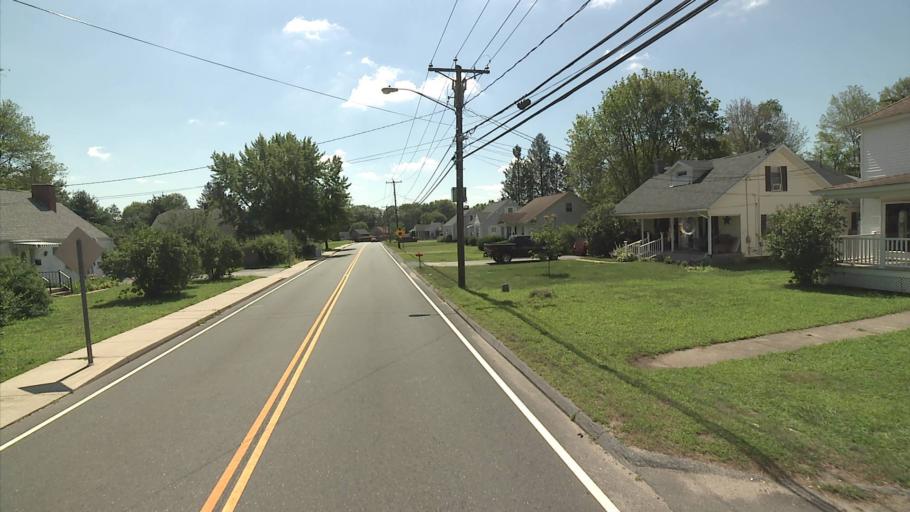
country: US
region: Connecticut
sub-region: Windham County
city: Plainfield Village
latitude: 41.6809
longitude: -71.9261
